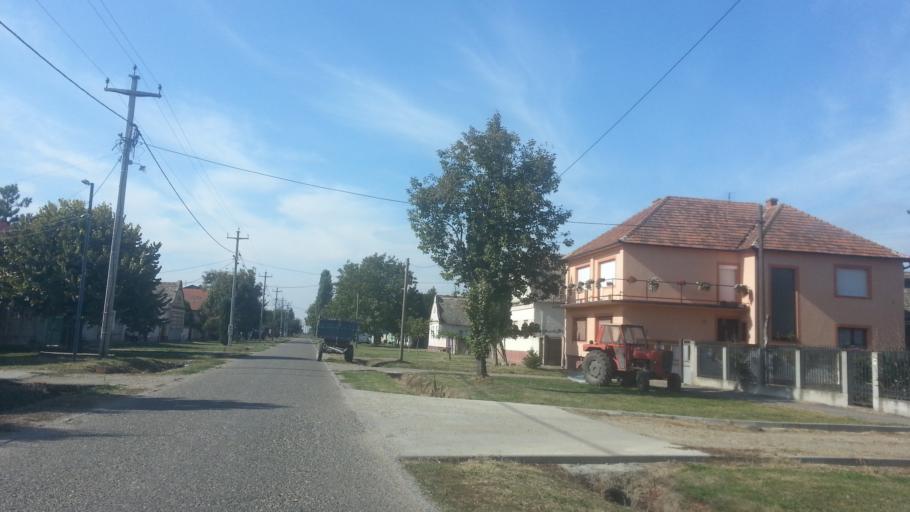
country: RS
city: Belegis
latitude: 45.0240
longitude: 20.3256
